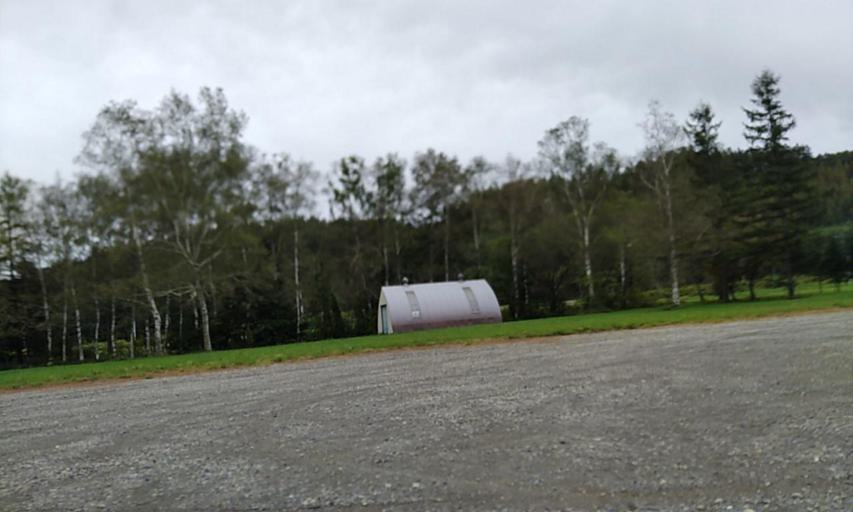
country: JP
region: Hokkaido
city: Obihiro
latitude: 42.6694
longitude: 143.0336
